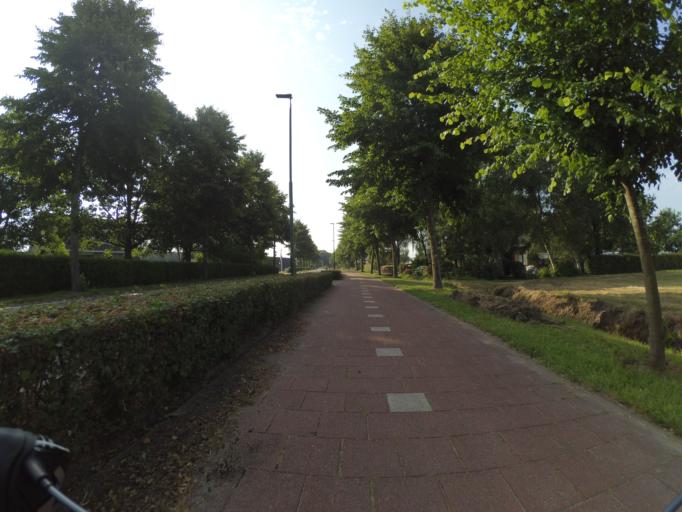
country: NL
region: North Brabant
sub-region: Gemeente Dongen
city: Dongen
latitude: 51.6396
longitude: 4.9547
